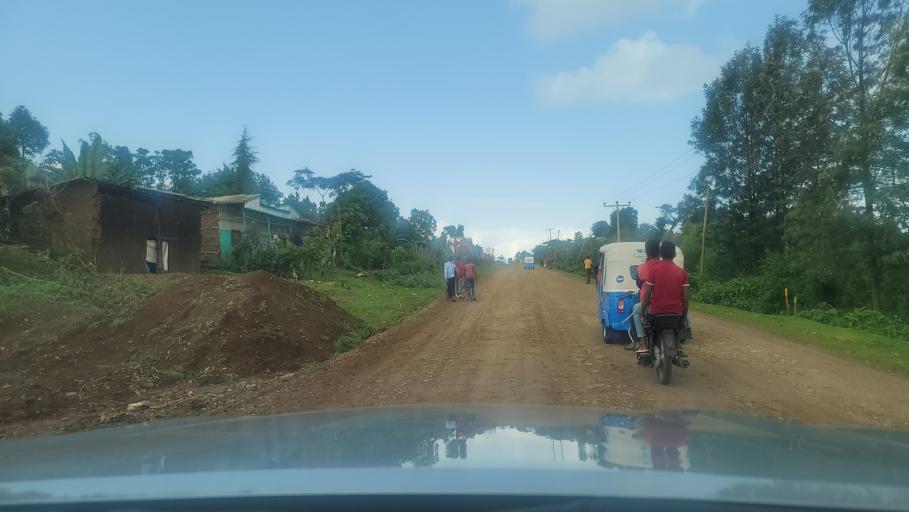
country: ET
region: Oromiya
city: Agaro
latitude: 7.8103
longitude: 36.5045
